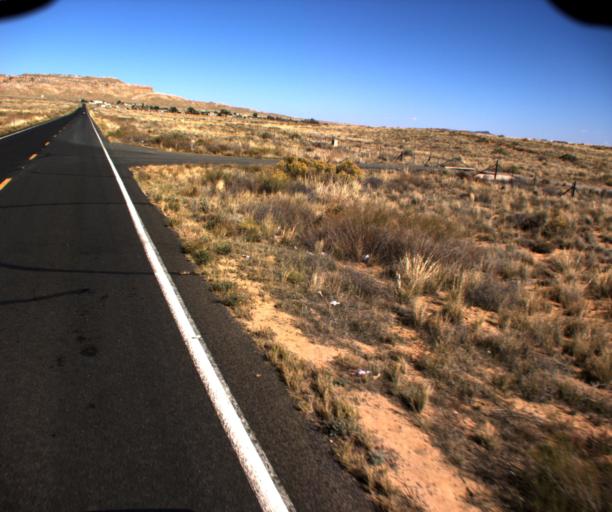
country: US
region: Arizona
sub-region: Navajo County
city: First Mesa
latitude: 35.7751
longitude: -110.5041
